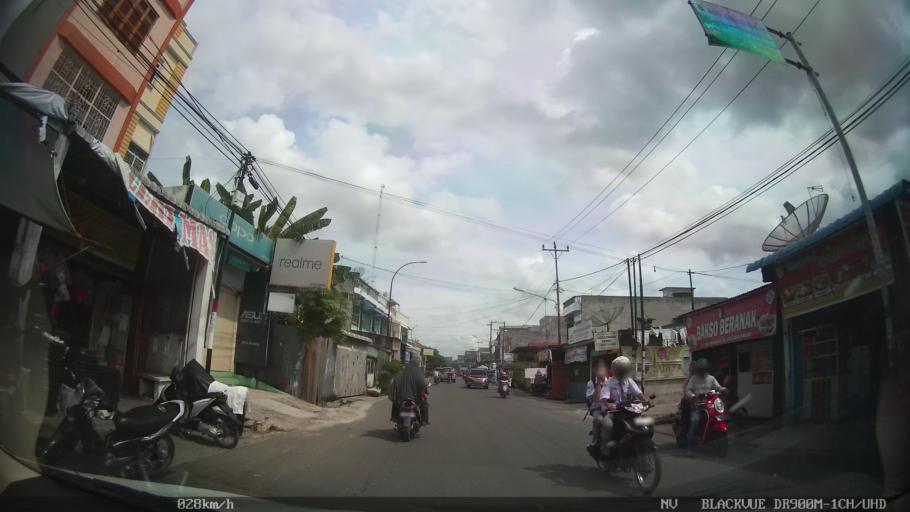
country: ID
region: North Sumatra
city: Percut
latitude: 3.5666
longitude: 98.8721
